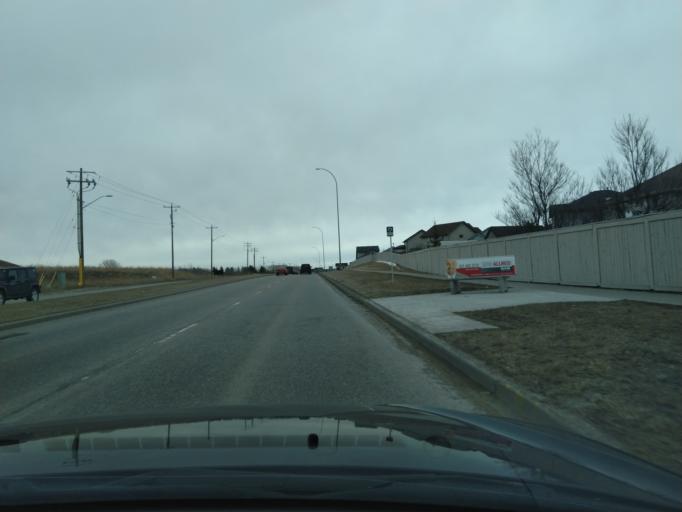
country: CA
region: Alberta
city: Calgary
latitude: 51.1541
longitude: -114.2284
